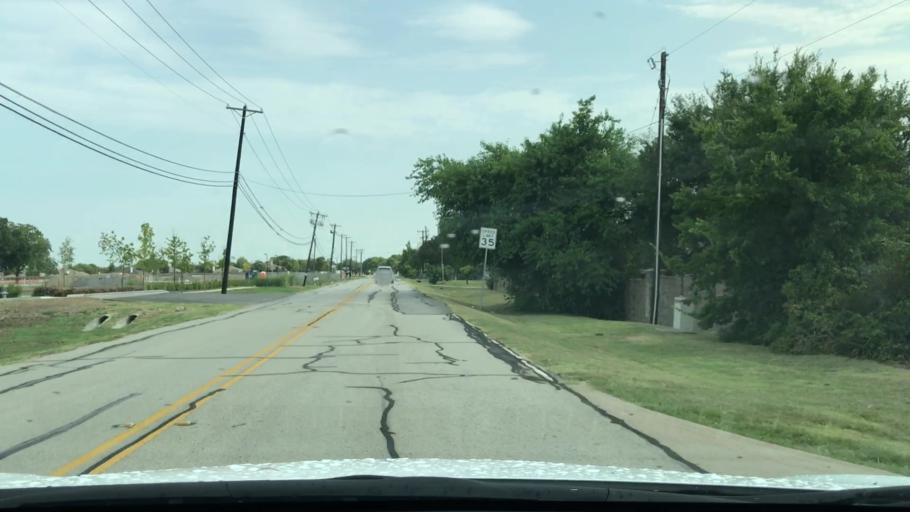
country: US
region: Texas
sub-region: Dallas County
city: Rowlett
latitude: 32.9301
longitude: -96.5364
